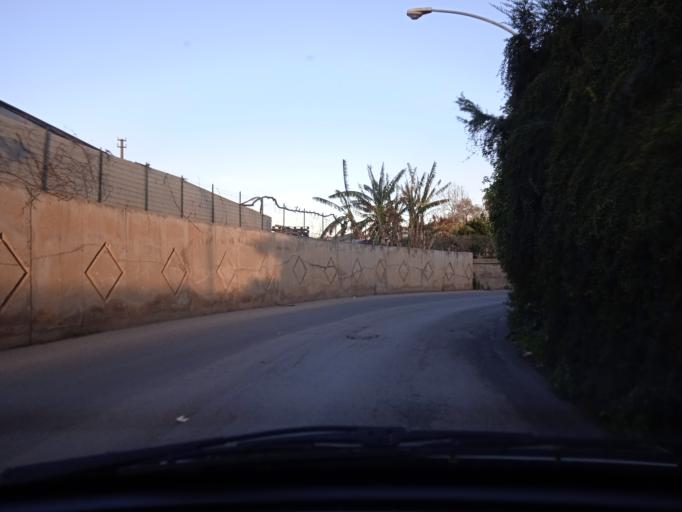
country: IT
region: Sicily
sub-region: Palermo
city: Ciaculli
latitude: 38.0867
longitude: 13.4234
